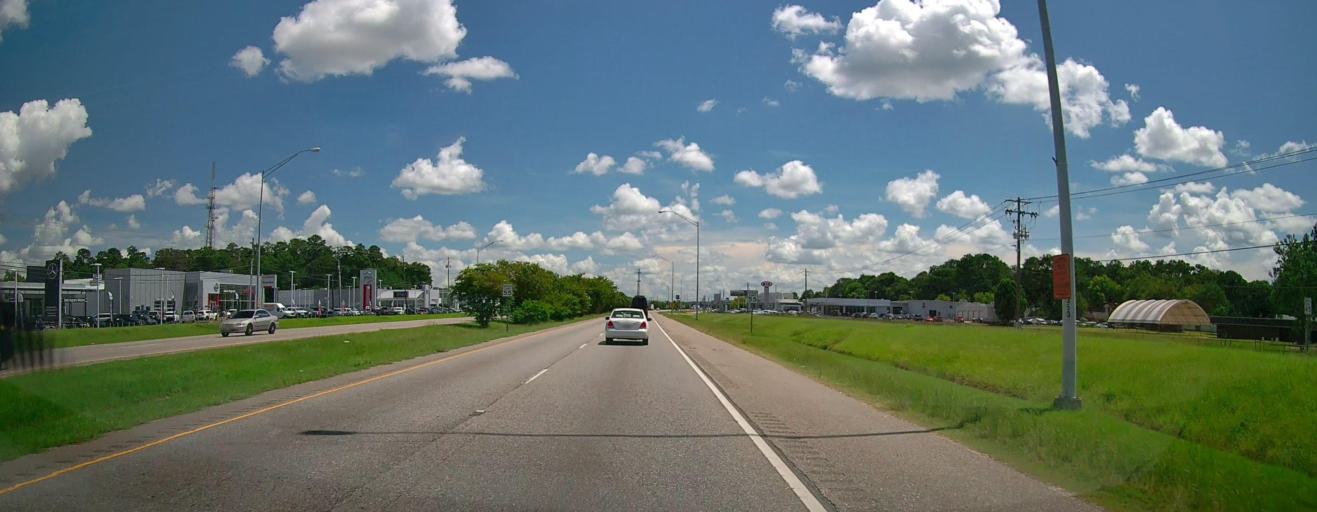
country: US
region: Alabama
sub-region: Montgomery County
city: Montgomery
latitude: 32.3783
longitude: -86.2098
